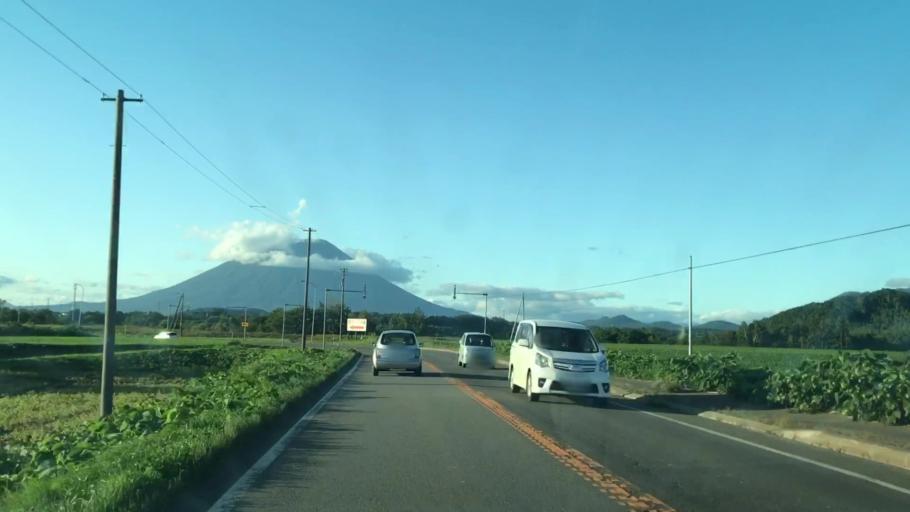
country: JP
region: Hokkaido
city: Niseko Town
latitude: 42.6773
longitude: 140.8417
